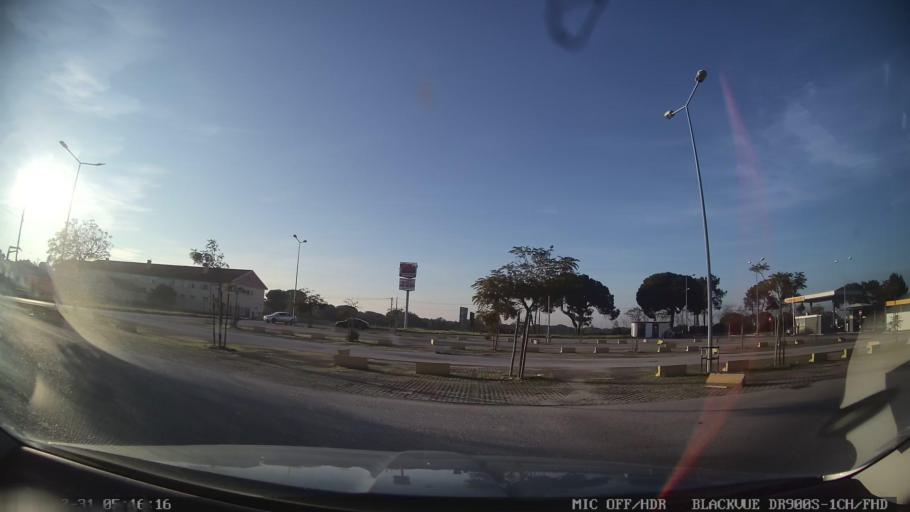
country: PT
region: Santarem
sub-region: Benavente
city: Benavente
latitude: 38.9610
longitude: -8.8199
